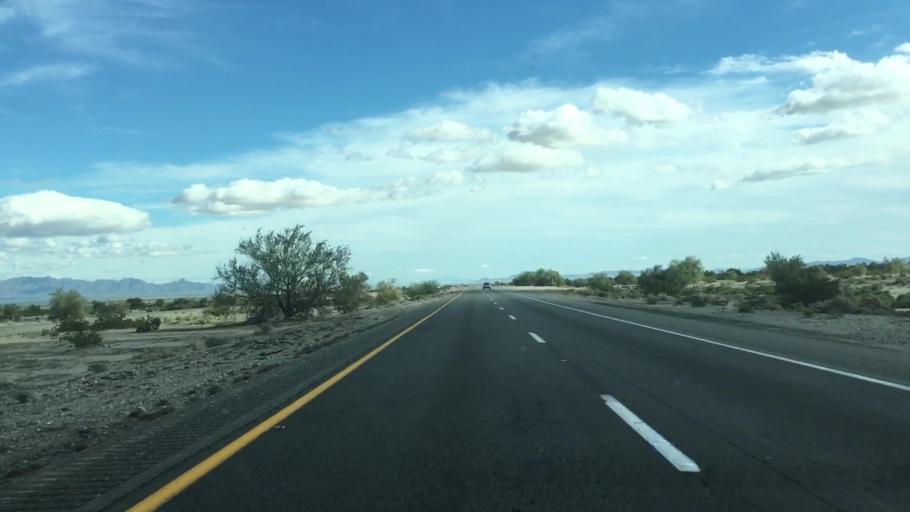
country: US
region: California
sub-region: Riverside County
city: Mesa Verde
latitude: 33.6587
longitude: -115.1636
